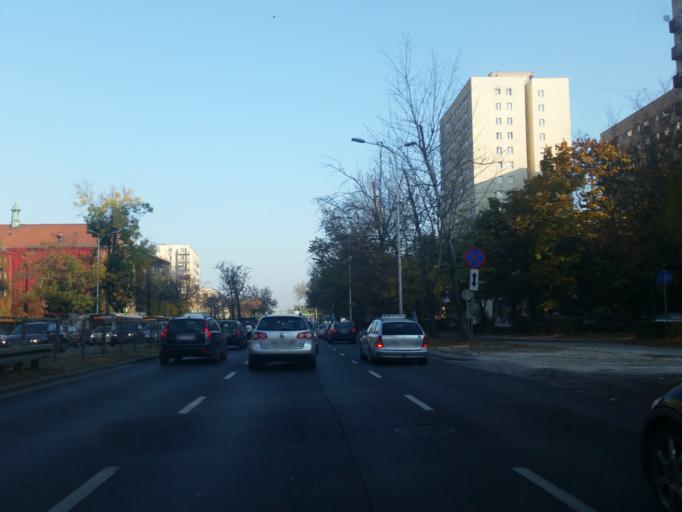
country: PL
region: Masovian Voivodeship
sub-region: Warszawa
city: Mokotow
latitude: 52.2091
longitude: 21.0482
